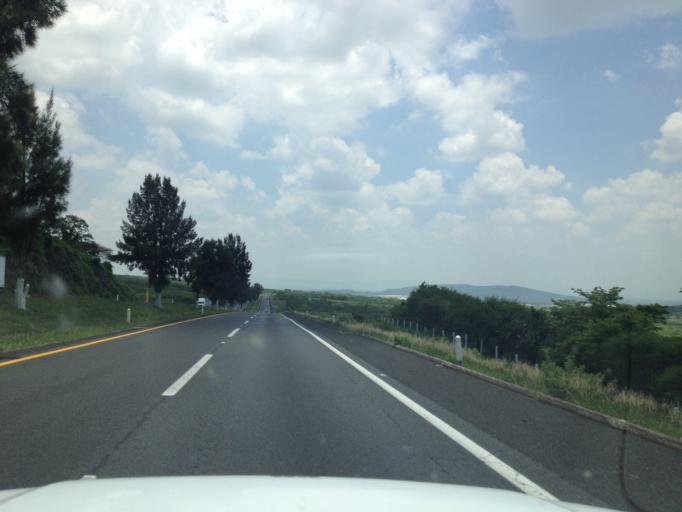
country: MX
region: Michoacan
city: Ixtlan
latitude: 20.2204
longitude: -102.3657
